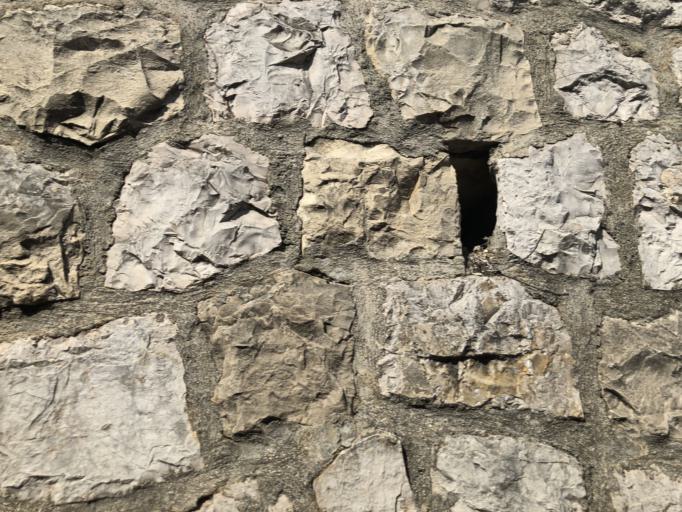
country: FR
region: Provence-Alpes-Cote d'Azur
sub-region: Departement des Alpes-Maritimes
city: Beaulieu-sur-Mer
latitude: 43.7103
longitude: 7.3251
